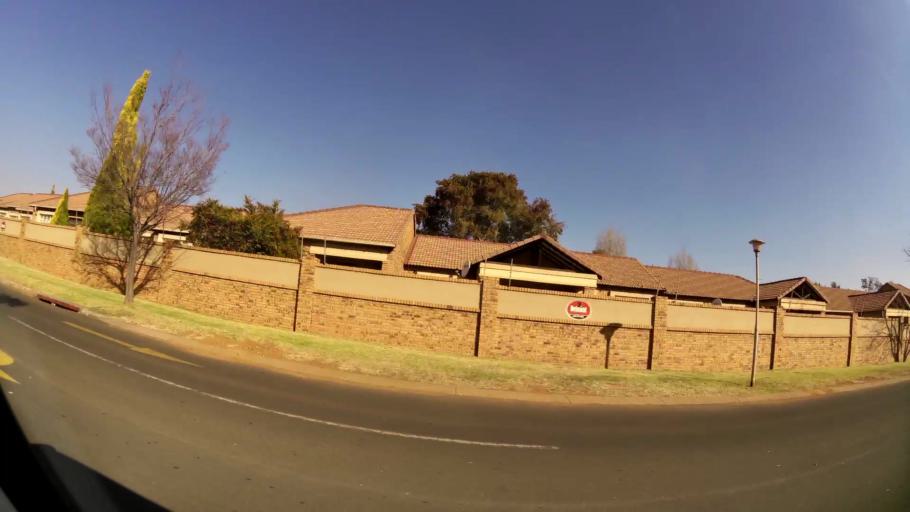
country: ZA
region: Gauteng
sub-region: City of Tshwane Metropolitan Municipality
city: Centurion
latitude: -25.8395
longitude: 28.3017
